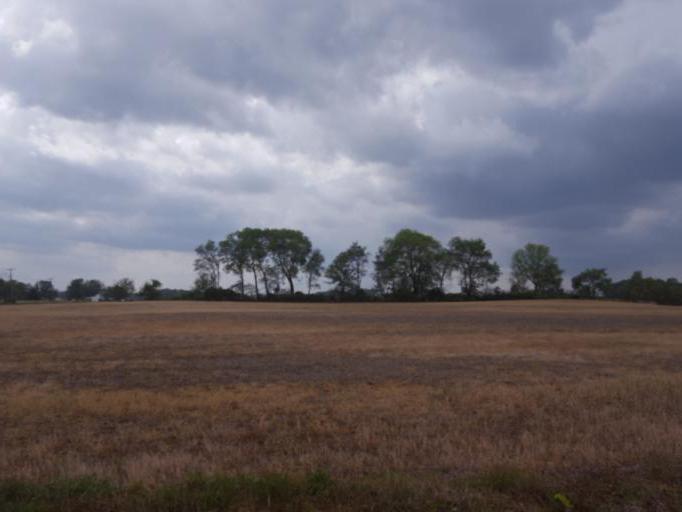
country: US
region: Ohio
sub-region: Licking County
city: Harbor Hills
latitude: 39.9186
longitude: -82.4372
